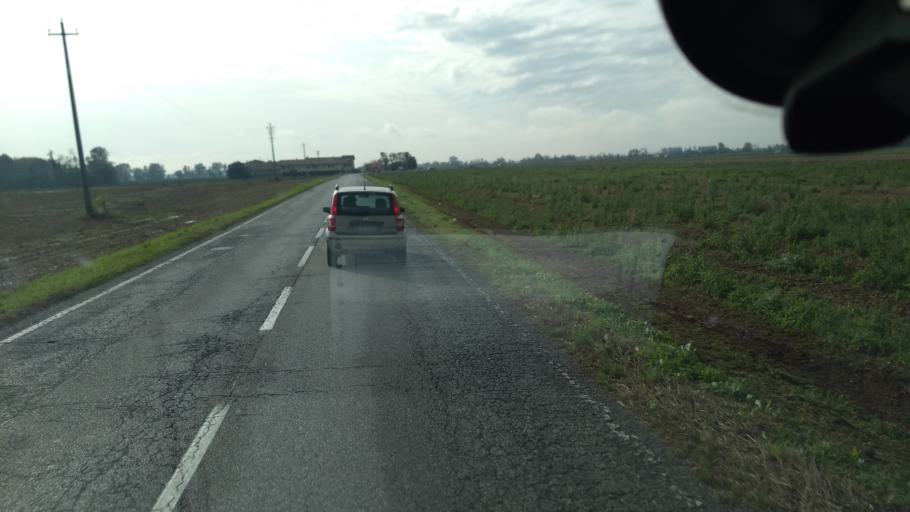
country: IT
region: Lombardy
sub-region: Provincia di Bergamo
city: Cologno al Serio
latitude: 45.5662
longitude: 9.6935
